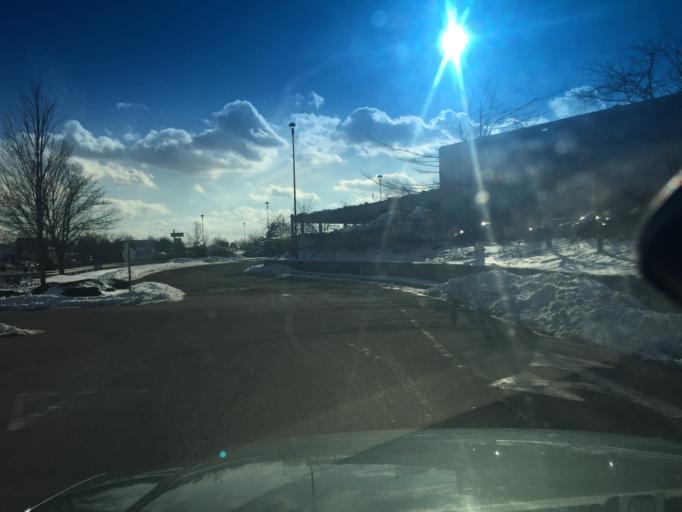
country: US
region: Rhode Island
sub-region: Providence County
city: Valley Falls
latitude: 41.9458
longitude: -71.3483
